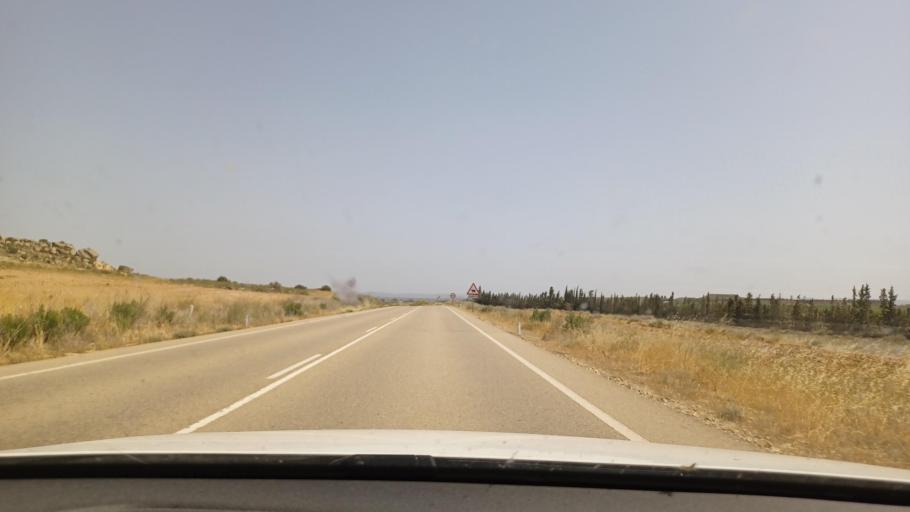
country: ES
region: Aragon
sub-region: Provincia de Zaragoza
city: Caspe
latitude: 41.2975
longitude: -0.0669
